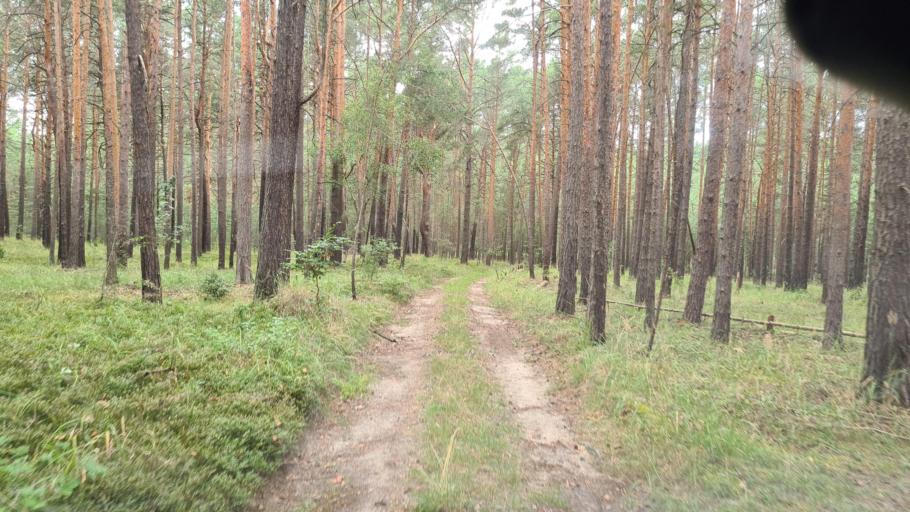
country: DE
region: Brandenburg
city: Sallgast
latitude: 51.5859
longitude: 13.8895
